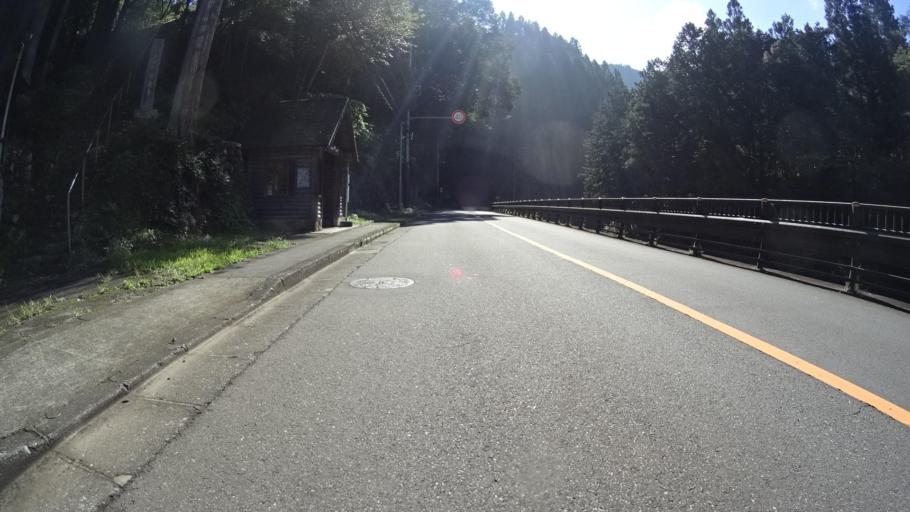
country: JP
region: Tokyo
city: Itsukaichi
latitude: 35.7357
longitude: 139.1249
